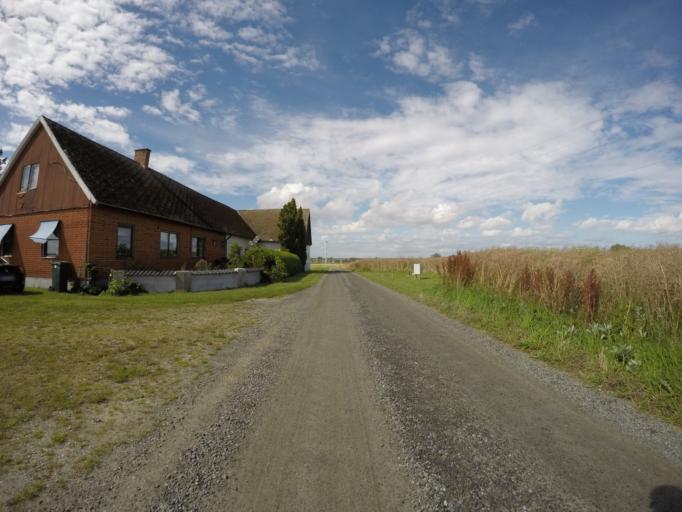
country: SE
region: Skane
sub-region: Tomelilla Kommun
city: Tomelilla
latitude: 55.4699
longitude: 14.1366
